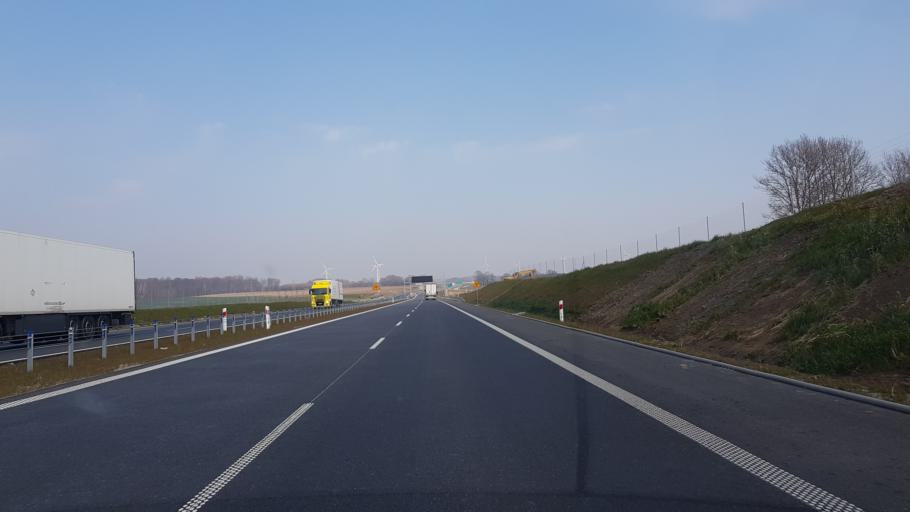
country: PL
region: West Pomeranian Voivodeship
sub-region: Powiat kolobrzeski
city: Dygowo
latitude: 54.1620
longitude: 15.7277
